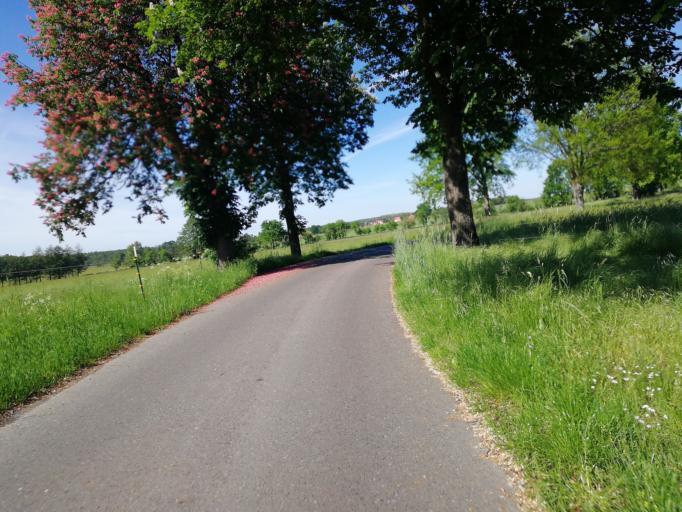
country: DE
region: Brandenburg
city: Calau
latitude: 51.7359
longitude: 13.9155
